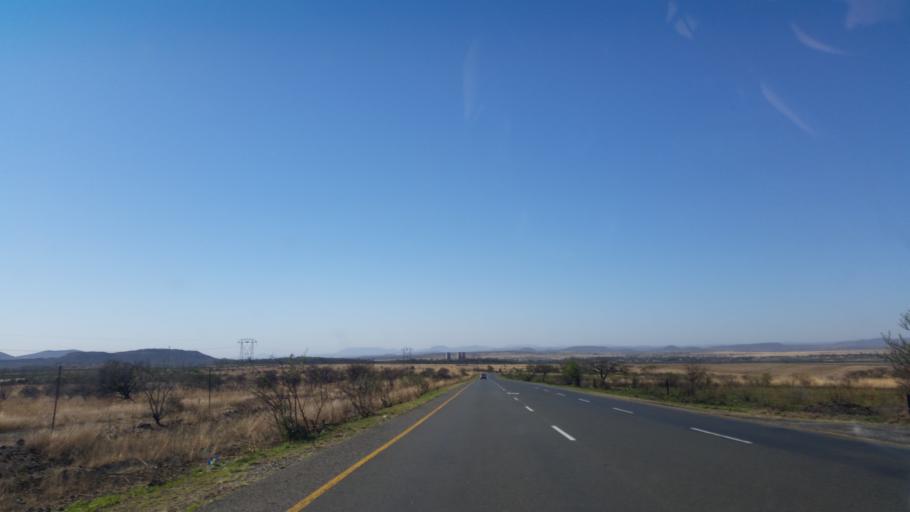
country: ZA
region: KwaZulu-Natal
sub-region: uThukela District Municipality
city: Ladysmith
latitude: -28.7112
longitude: 29.7918
